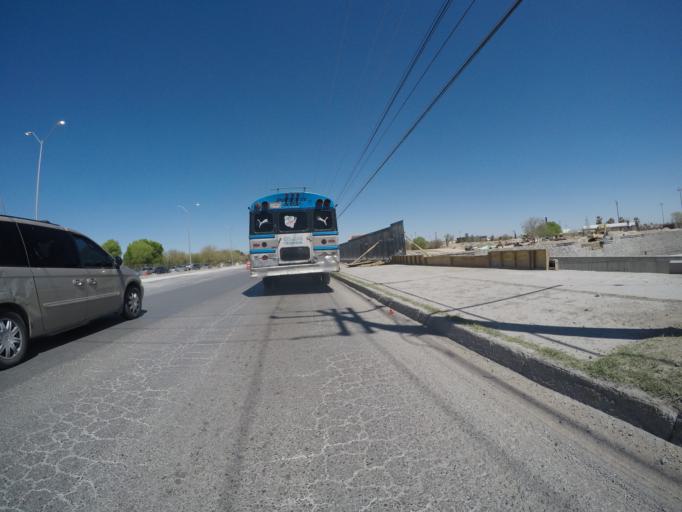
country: MX
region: Chihuahua
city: Ciudad Juarez
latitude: 31.6850
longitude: -106.4244
